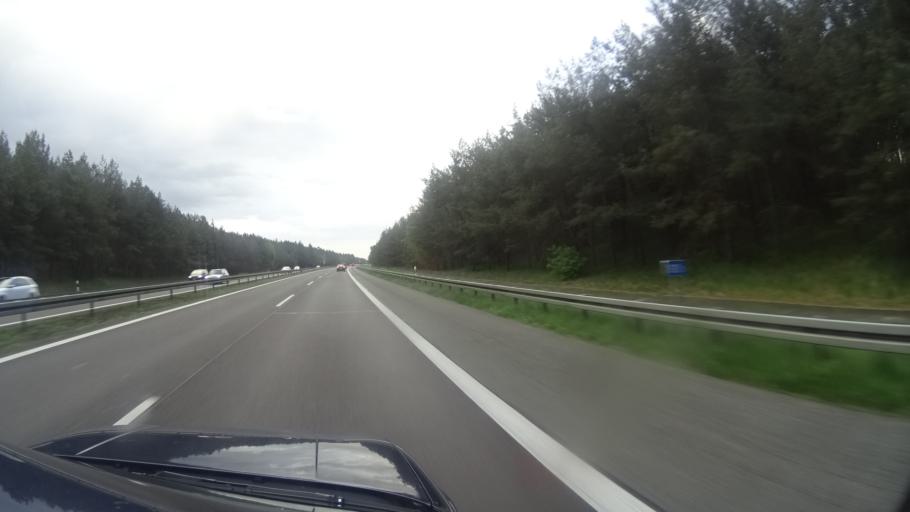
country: DE
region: Brandenburg
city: Walsleben
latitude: 53.0338
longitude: 12.5657
